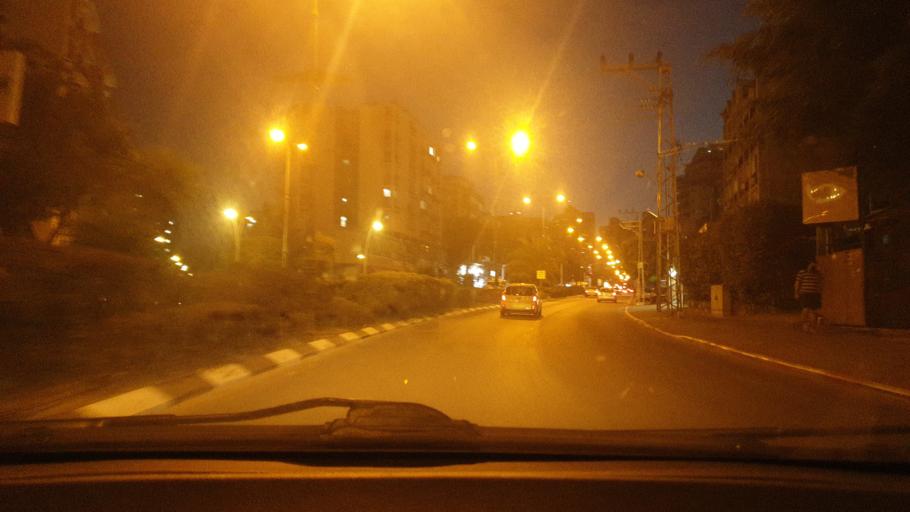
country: IL
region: Central District
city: Rishon LeZiyyon
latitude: 31.9715
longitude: 34.8062
